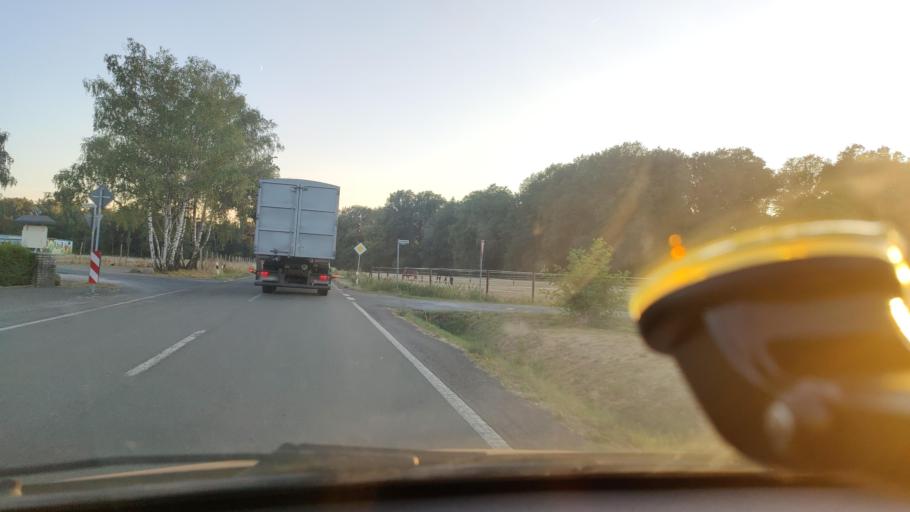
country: DE
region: North Rhine-Westphalia
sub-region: Regierungsbezirk Munster
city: Klein Reken
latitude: 51.7820
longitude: 7.0156
